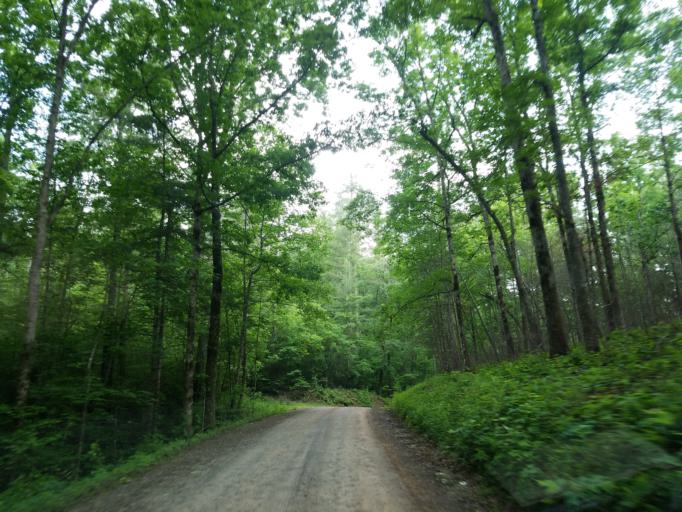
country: US
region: Georgia
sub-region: Lumpkin County
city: Dahlonega
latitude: 34.5950
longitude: -84.1168
